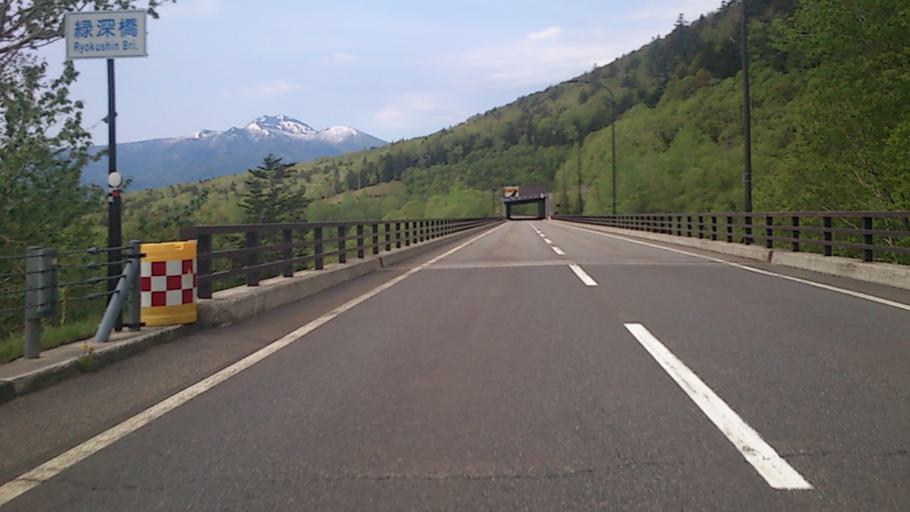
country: JP
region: Hokkaido
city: Kamikawa
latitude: 43.5714
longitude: 143.1209
